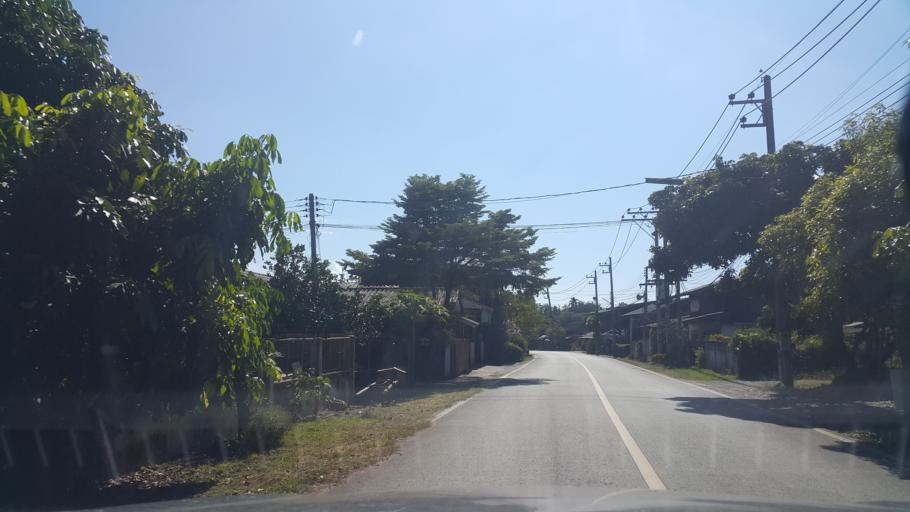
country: TH
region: Chiang Mai
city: Mae On
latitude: 18.7876
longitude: 99.2575
